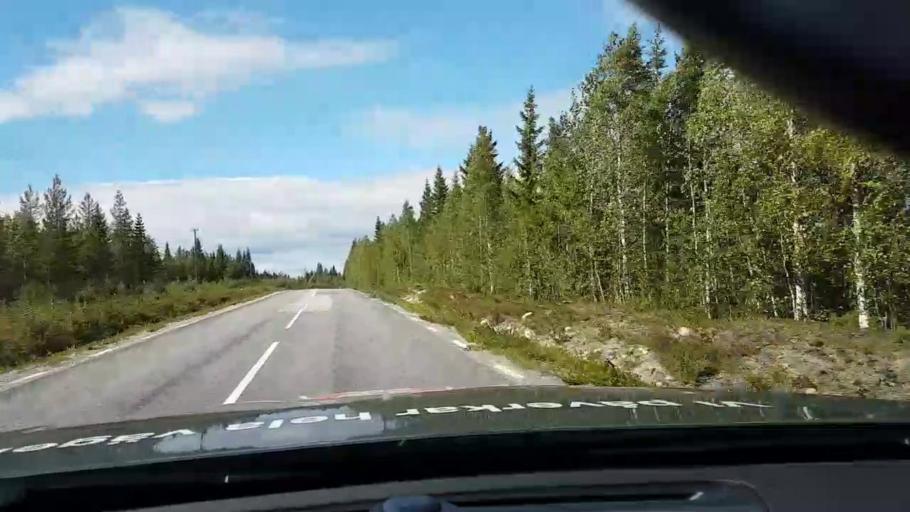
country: SE
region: Vaesterbotten
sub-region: Asele Kommun
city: Asele
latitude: 63.8198
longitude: 17.4905
